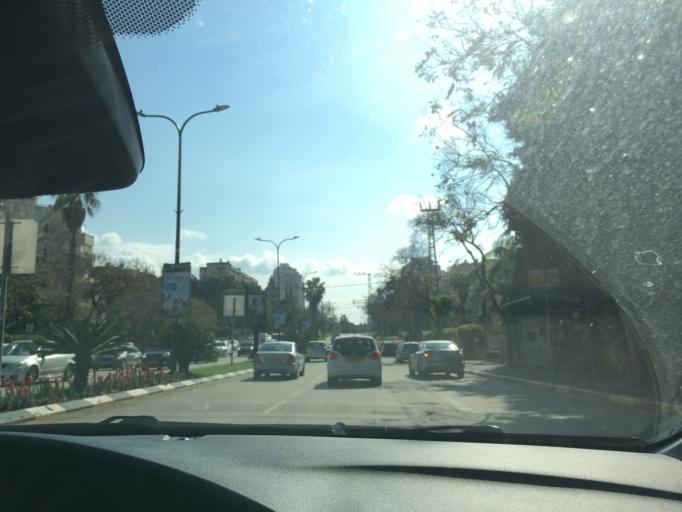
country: IL
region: Tel Aviv
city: Ramat HaSharon
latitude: 32.1558
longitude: 34.8422
